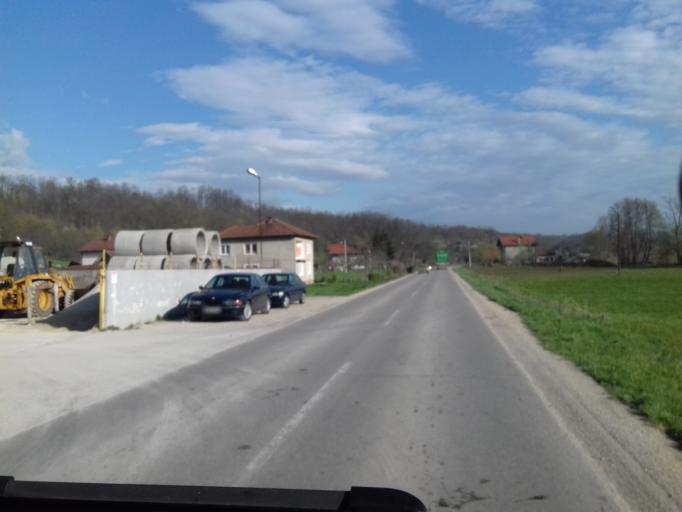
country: BA
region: Federation of Bosnia and Herzegovina
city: Tesanjka
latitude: 44.6498
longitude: 18.0174
